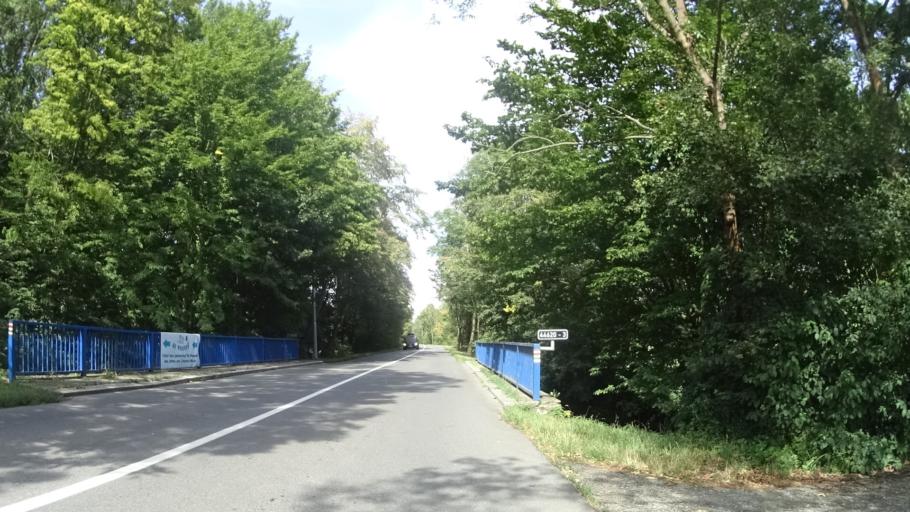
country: CZ
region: Olomoucky
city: Naklo
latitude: 49.6796
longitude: 17.1458
